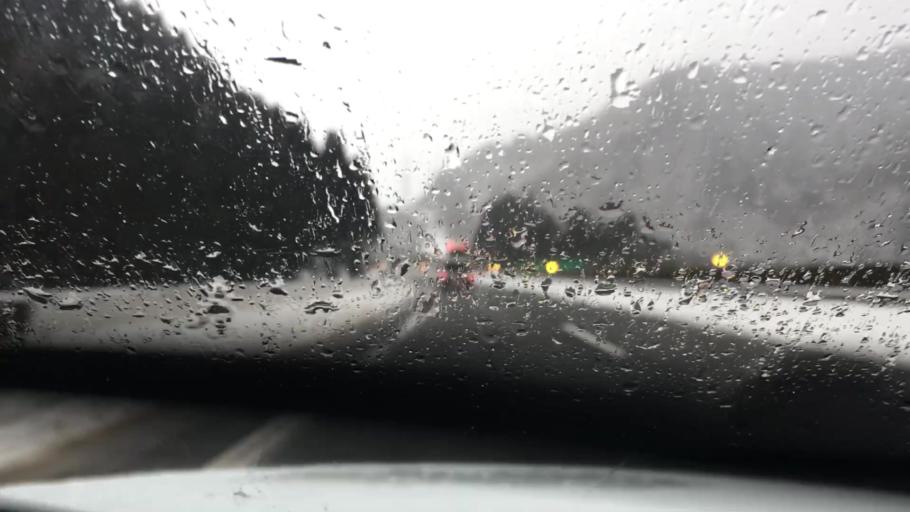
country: JP
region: Akita
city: Hanawa
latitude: 40.1351
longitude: 140.8159
